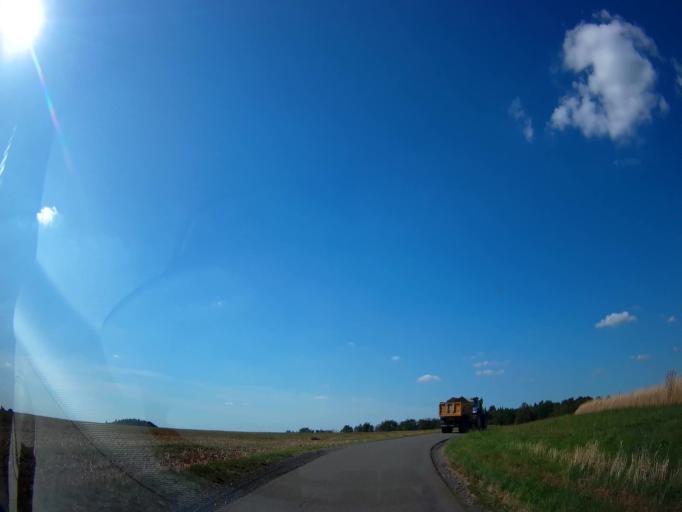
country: BE
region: Wallonia
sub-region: Province de Namur
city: Dinant
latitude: 50.2369
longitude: 4.9678
